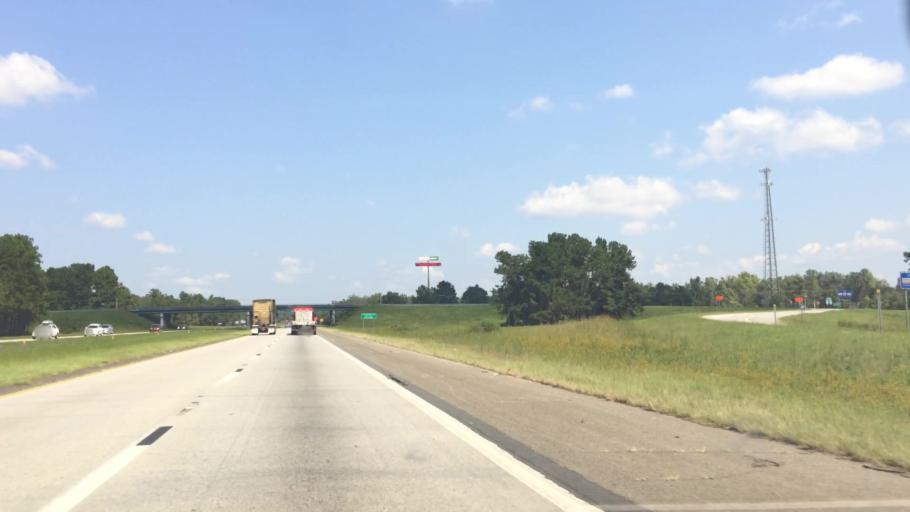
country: US
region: South Carolina
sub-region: Dorchester County
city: Saint George
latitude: 33.0820
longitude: -80.6538
